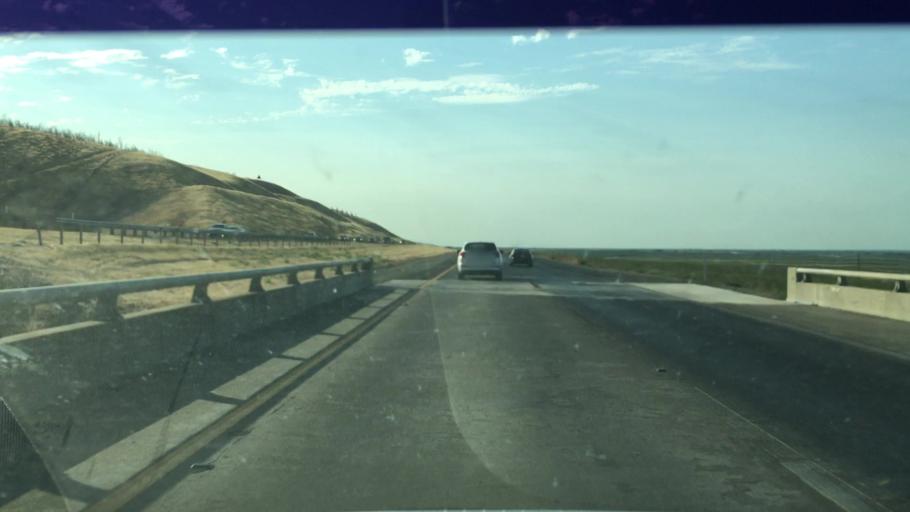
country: US
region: California
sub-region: Stanislaus County
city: Patterson
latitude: 37.4797
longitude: -121.1955
